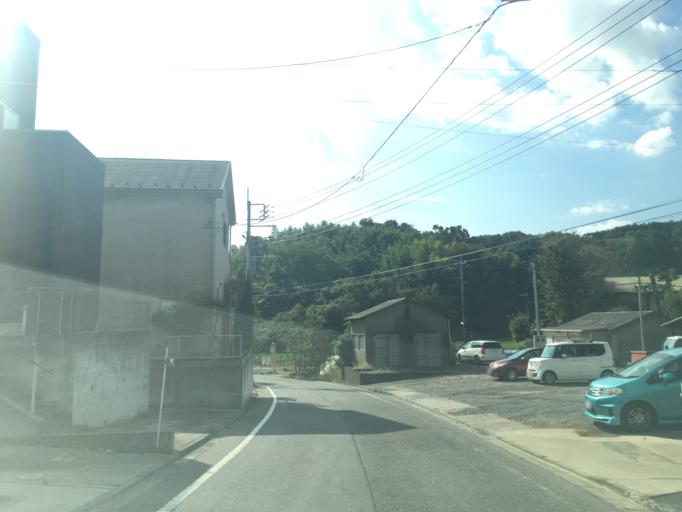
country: JP
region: Tokyo
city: Hino
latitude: 35.6094
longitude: 139.4073
